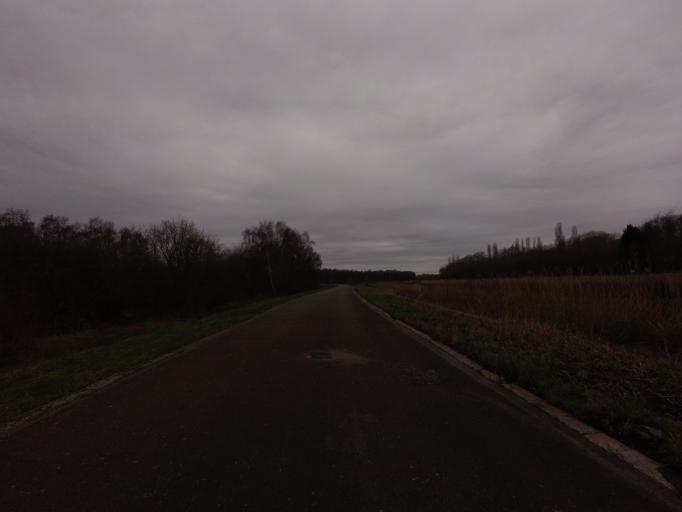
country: BE
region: Flanders
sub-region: Provincie Antwerpen
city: Duffel
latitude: 51.1112
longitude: 4.5334
